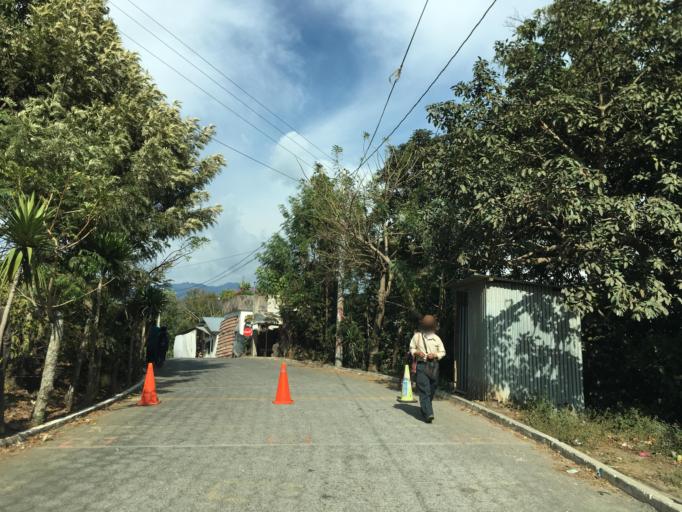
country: GT
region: Solola
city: San Antonio Palopo
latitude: 14.6582
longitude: -91.1578
